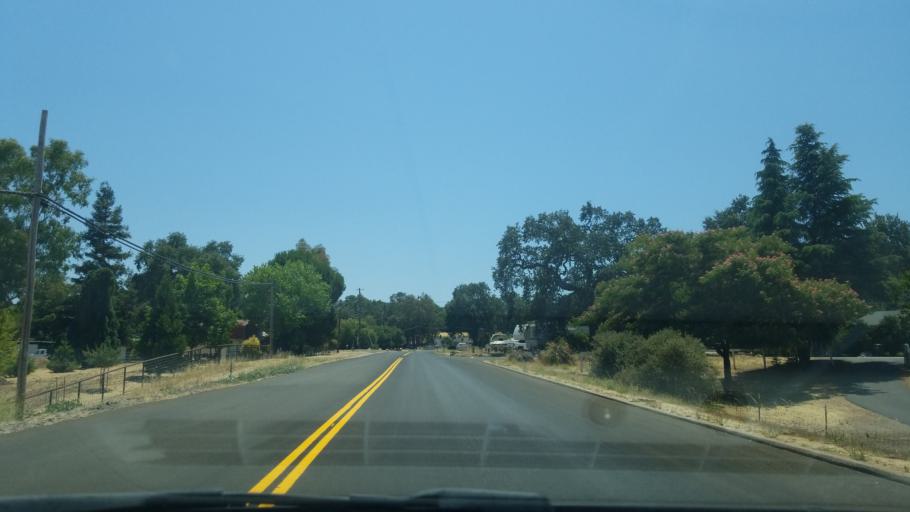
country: US
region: California
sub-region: San Luis Obispo County
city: Atascadero
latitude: 35.4883
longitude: -120.6479
